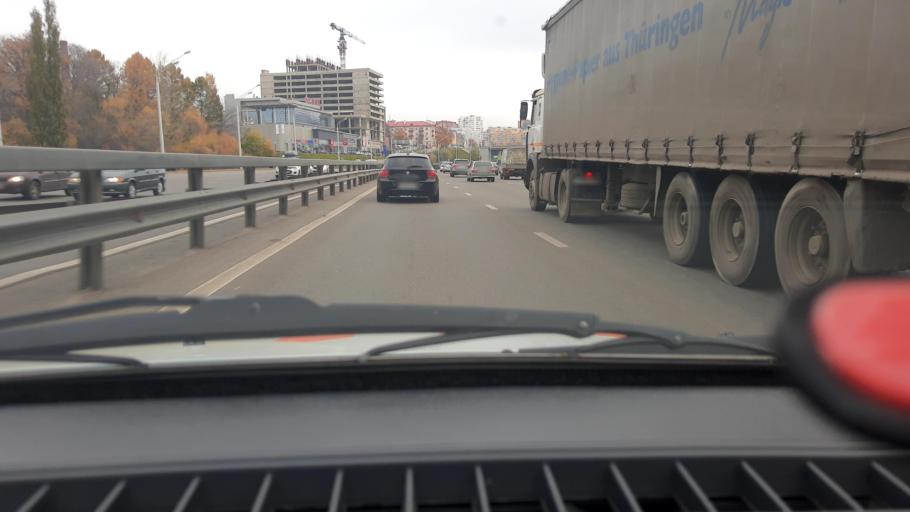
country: RU
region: Bashkortostan
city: Ufa
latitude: 54.7470
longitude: 56.0134
